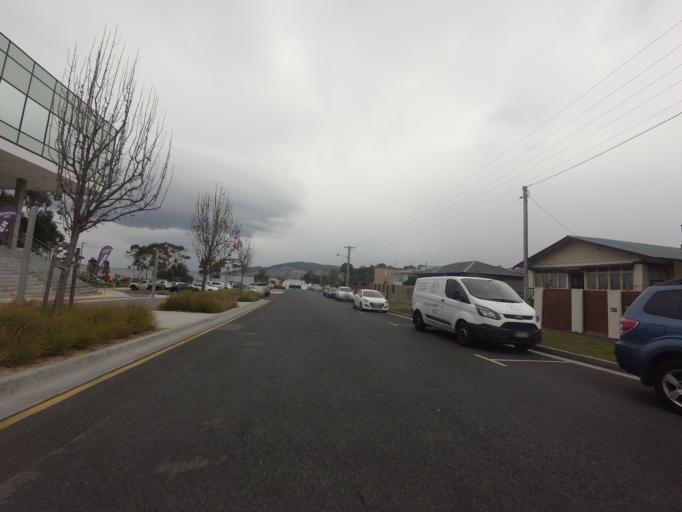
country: AU
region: Tasmania
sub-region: Clarence
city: Bellerive
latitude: -42.8775
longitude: 147.3720
